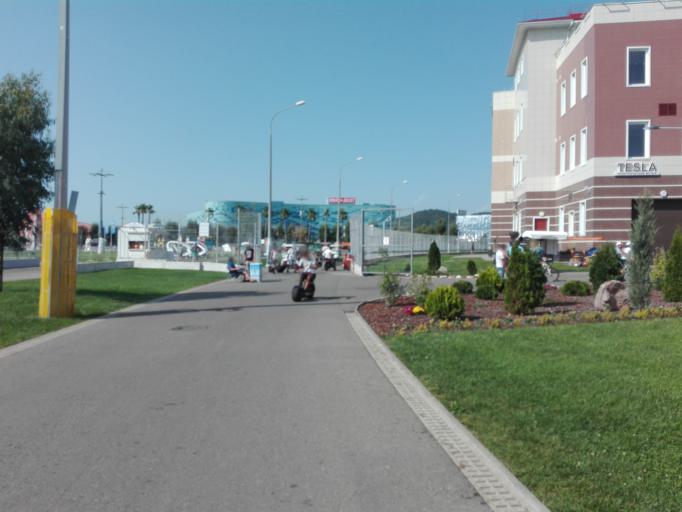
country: RU
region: Krasnodarskiy
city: Adler
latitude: 43.4034
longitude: 39.9604
